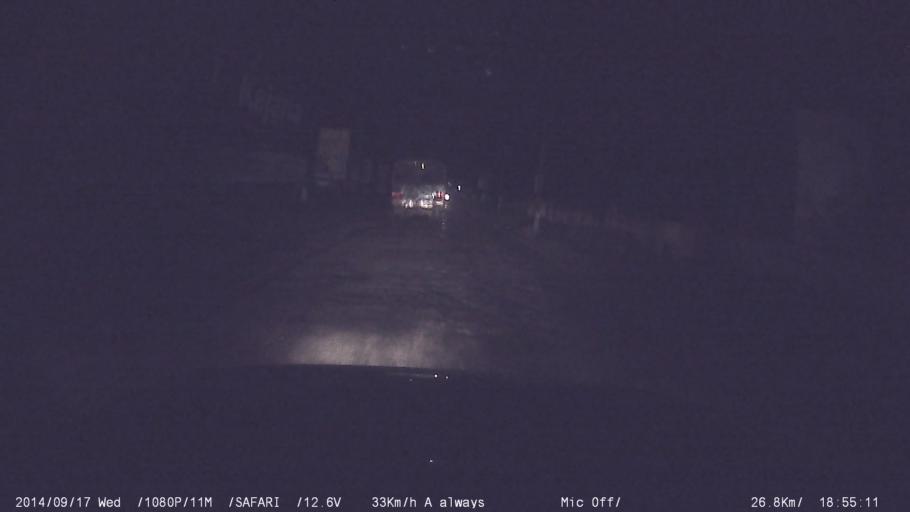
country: IN
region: Kerala
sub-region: Kottayam
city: Kottayam
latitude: 9.5397
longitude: 76.5136
